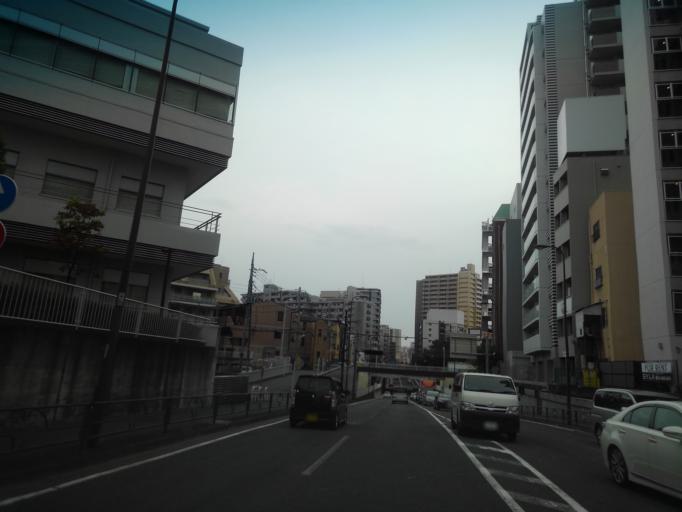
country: JP
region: Tokyo
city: Hino
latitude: 35.6997
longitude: 139.4180
